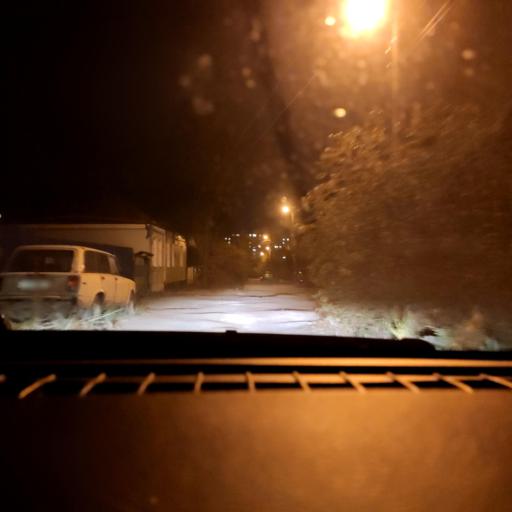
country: RU
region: Voronezj
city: Voronezh
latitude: 51.6968
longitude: 39.2629
